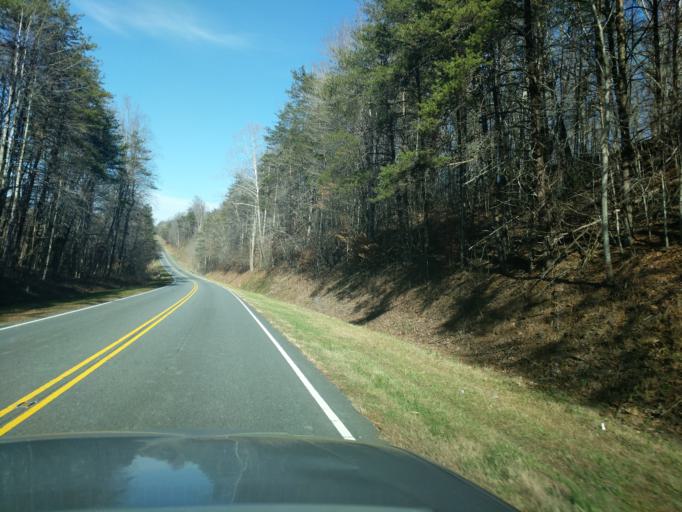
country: US
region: North Carolina
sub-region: Rutherford County
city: Rutherfordton
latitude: 35.4567
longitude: -81.9788
